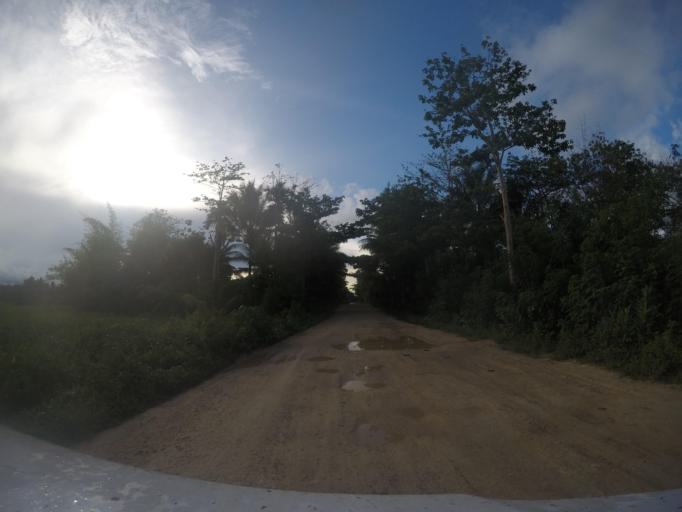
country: TL
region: Lautem
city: Lospalos
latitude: -8.5006
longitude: 127.0013
